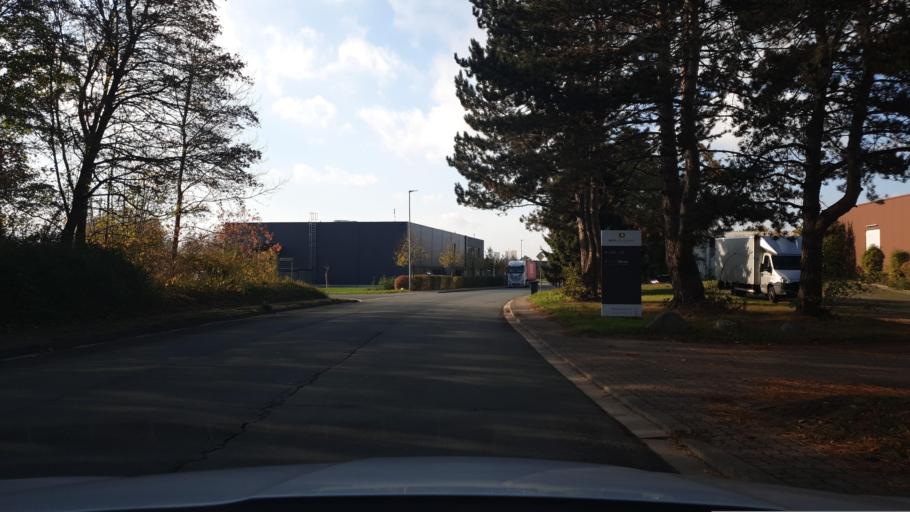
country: DE
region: North Rhine-Westphalia
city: Bad Oeynhausen
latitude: 52.2322
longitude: 8.8081
